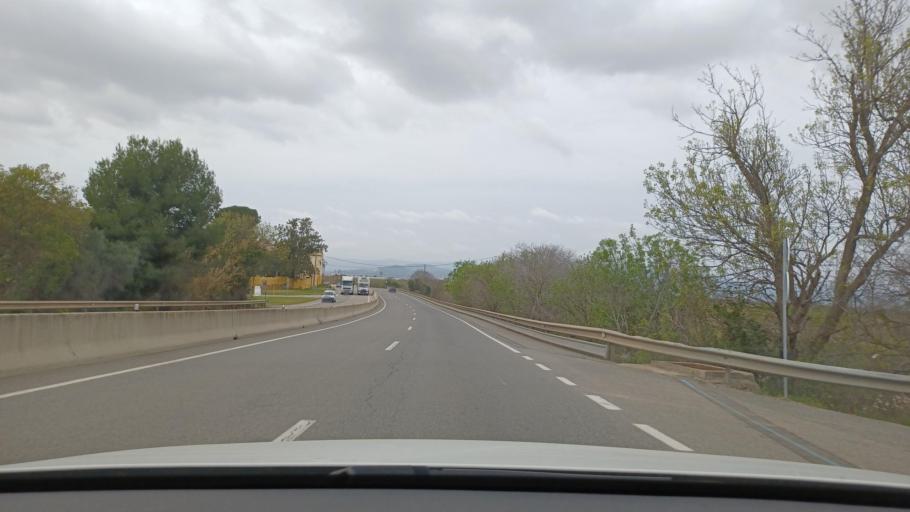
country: ES
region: Catalonia
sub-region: Provincia de Tarragona
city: Vila-seca
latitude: 41.1269
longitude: 1.1530
